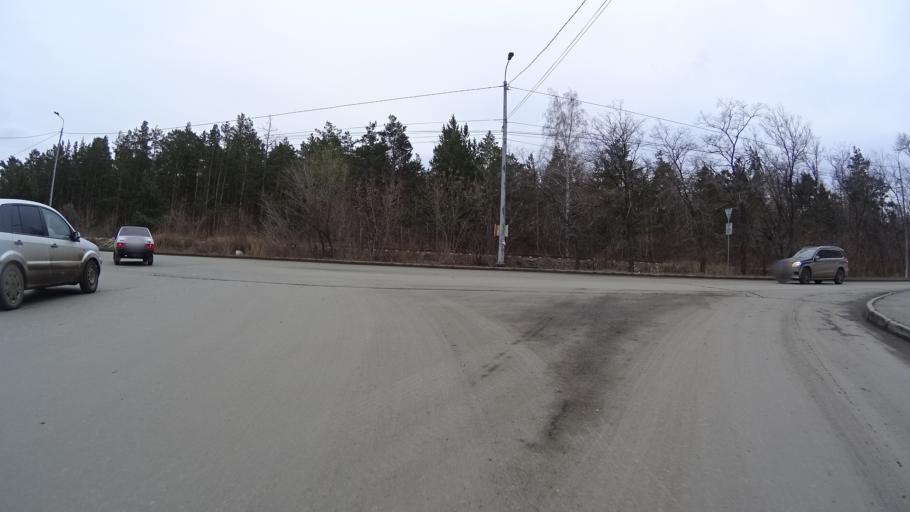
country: RU
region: Chelyabinsk
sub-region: Gorod Chelyabinsk
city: Chelyabinsk
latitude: 55.1691
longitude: 61.3542
